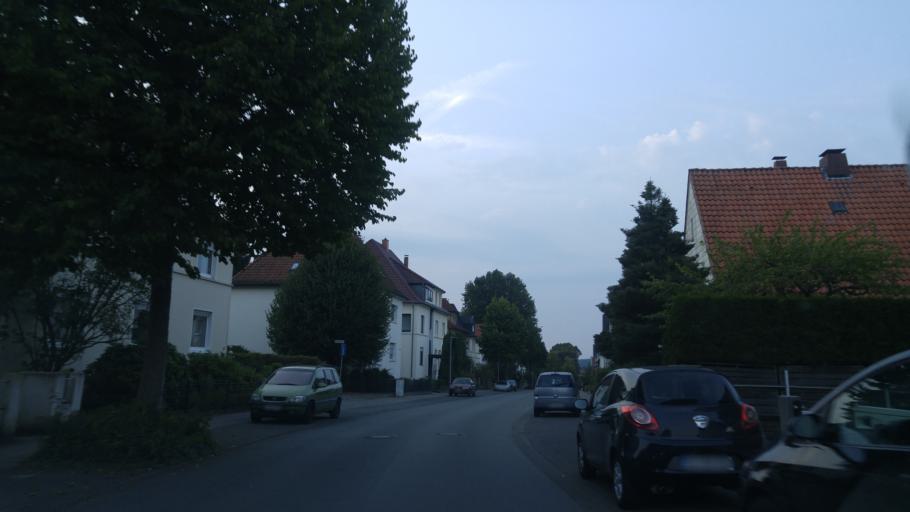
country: DE
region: North Rhine-Westphalia
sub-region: Regierungsbezirk Detmold
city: Bielefeld
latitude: 52.0521
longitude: 8.5498
